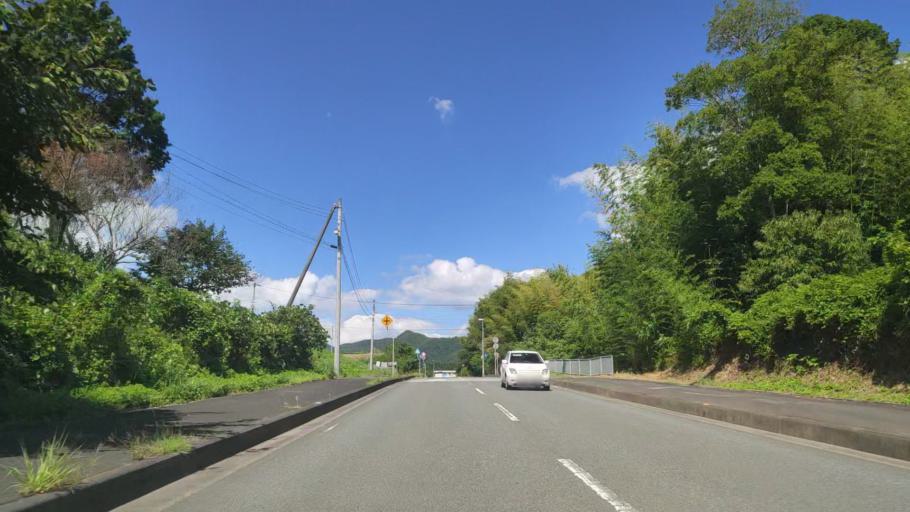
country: JP
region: Kyoto
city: Fukuchiyama
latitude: 35.2310
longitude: 135.1283
